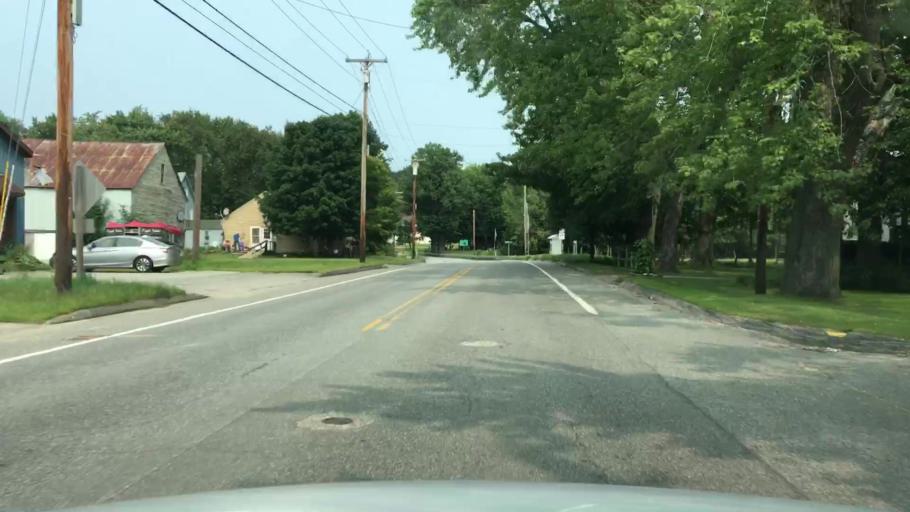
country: US
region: Maine
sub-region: Androscoggin County
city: Livermore Falls
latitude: 44.4610
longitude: -70.1771
